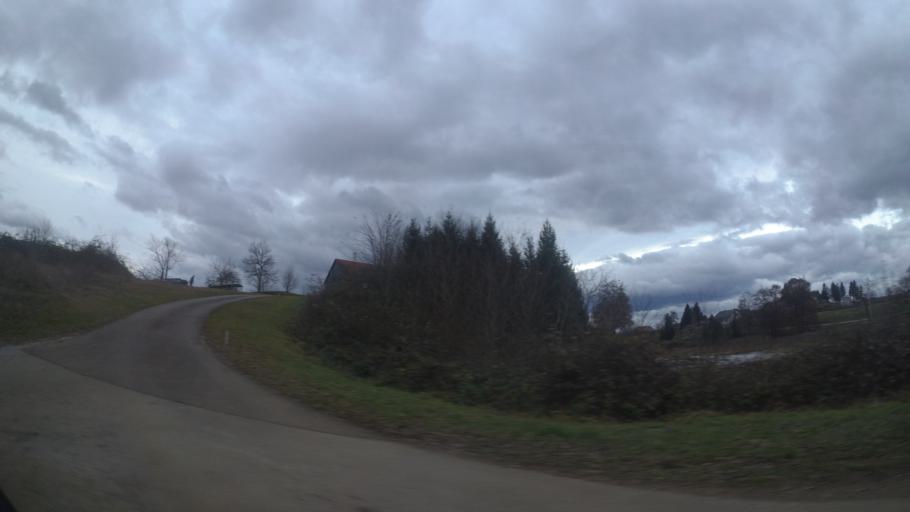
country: HR
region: Karlovacka
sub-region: Grad Karlovac
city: Karlovac
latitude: 45.3937
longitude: 15.5232
